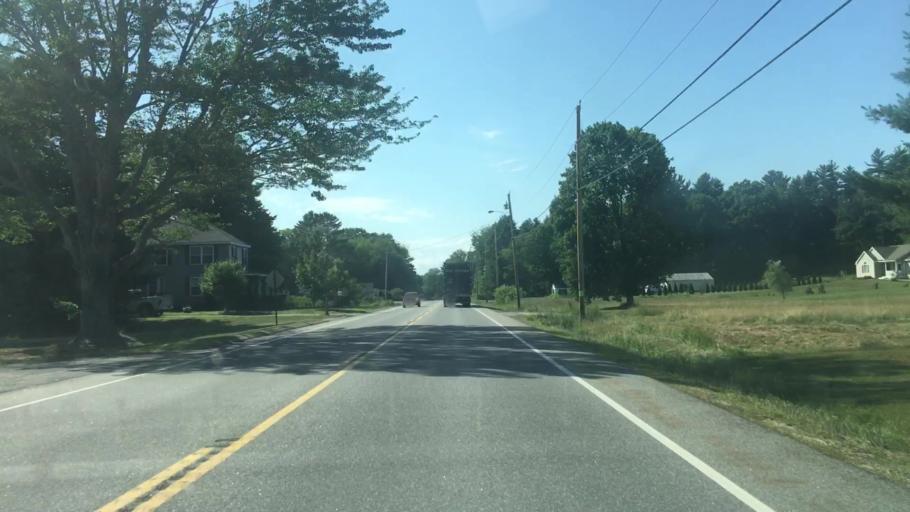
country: US
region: Maine
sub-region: York County
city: Buxton
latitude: 43.5677
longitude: -70.5056
